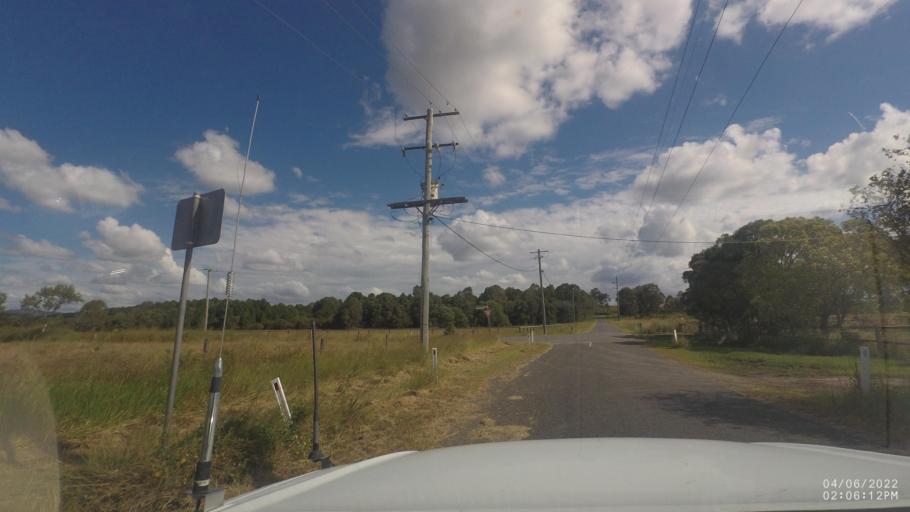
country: AU
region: Queensland
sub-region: Logan
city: Chambers Flat
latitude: -27.7668
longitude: 153.0637
